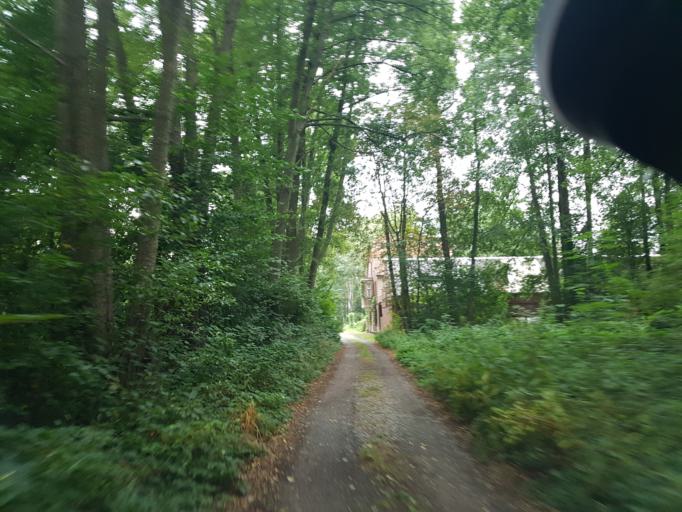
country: DE
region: Brandenburg
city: Ruckersdorf
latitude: 51.6019
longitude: 13.5692
